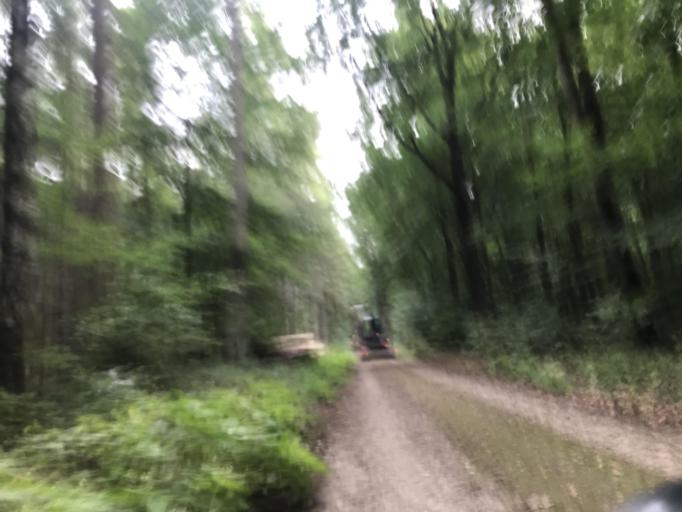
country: DE
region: Lower Saxony
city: Vastorf
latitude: 53.2154
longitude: 10.5425
